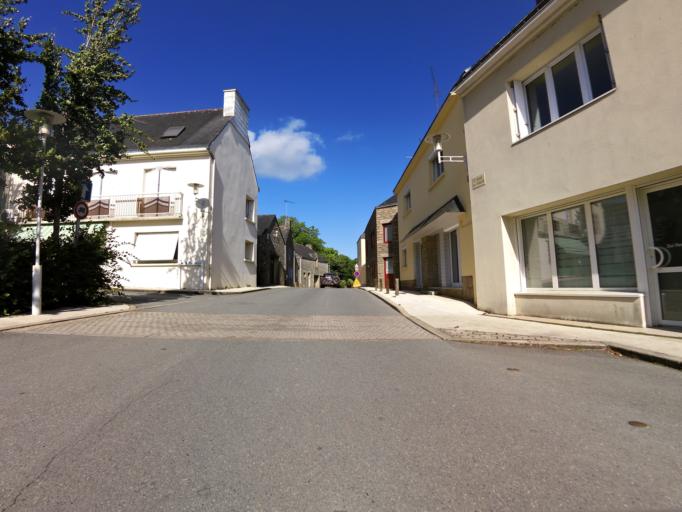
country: FR
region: Brittany
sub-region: Departement du Morbihan
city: Caden
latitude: 47.6307
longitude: -2.2869
